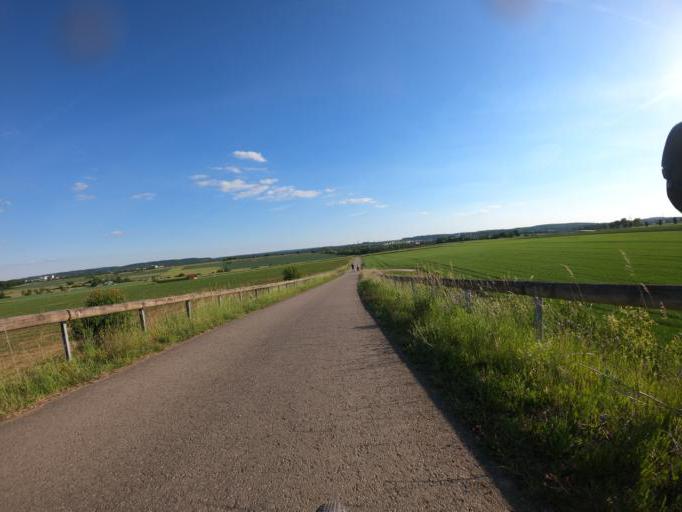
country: DE
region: Baden-Wuerttemberg
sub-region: Regierungsbezirk Stuttgart
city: Magstadt
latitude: 48.7086
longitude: 8.9552
